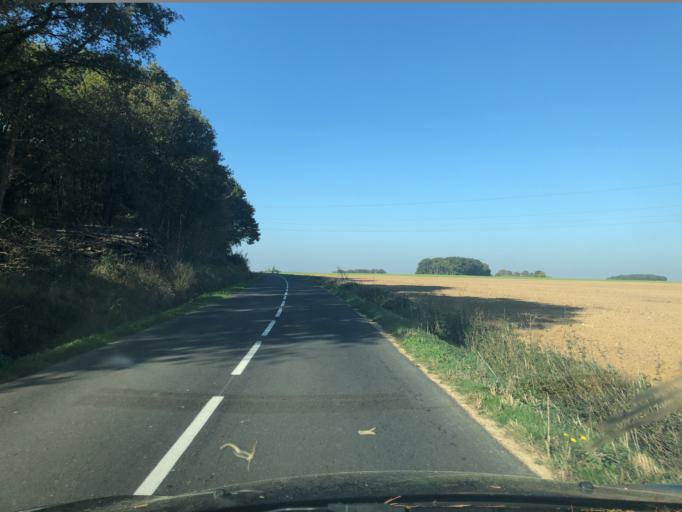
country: FR
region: Centre
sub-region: Departement d'Indre-et-Loire
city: Rouziers-de-Touraine
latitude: 47.5352
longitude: 0.6370
